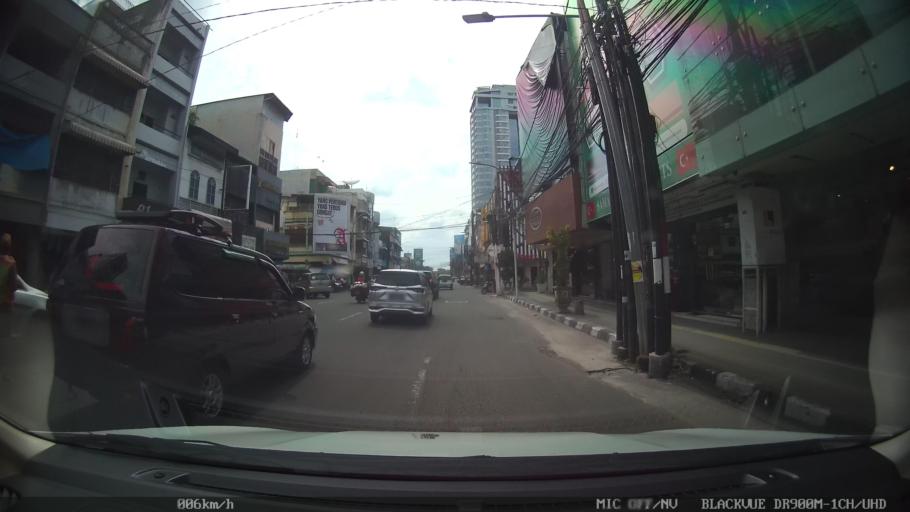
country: ID
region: North Sumatra
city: Medan
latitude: 3.5840
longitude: 98.6695
